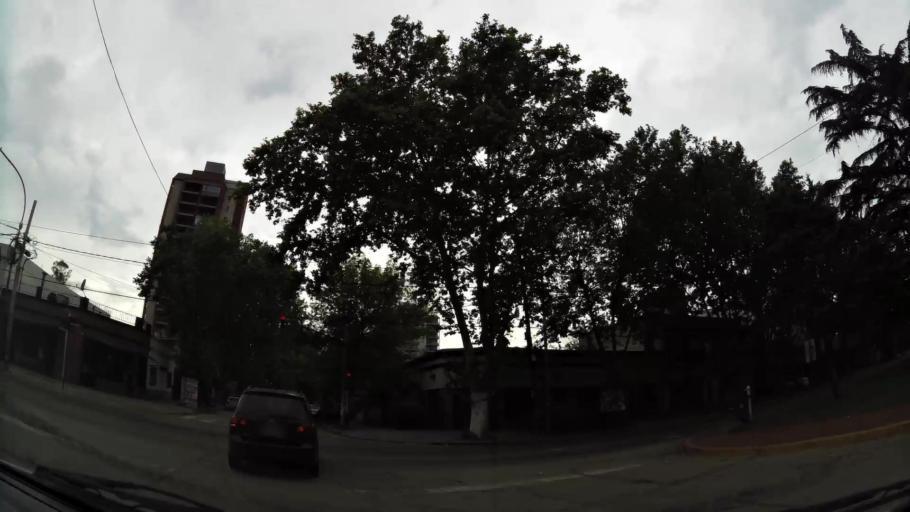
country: AR
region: Buenos Aires
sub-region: Partido de Quilmes
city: Quilmes
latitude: -34.8049
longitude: -58.2783
